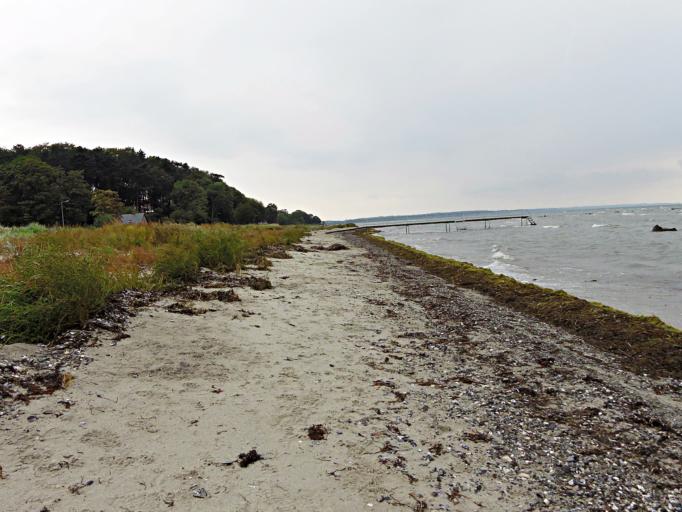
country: DK
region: Capital Region
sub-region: Fredensborg Kommune
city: Kokkedal
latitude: 55.9043
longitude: 12.5295
